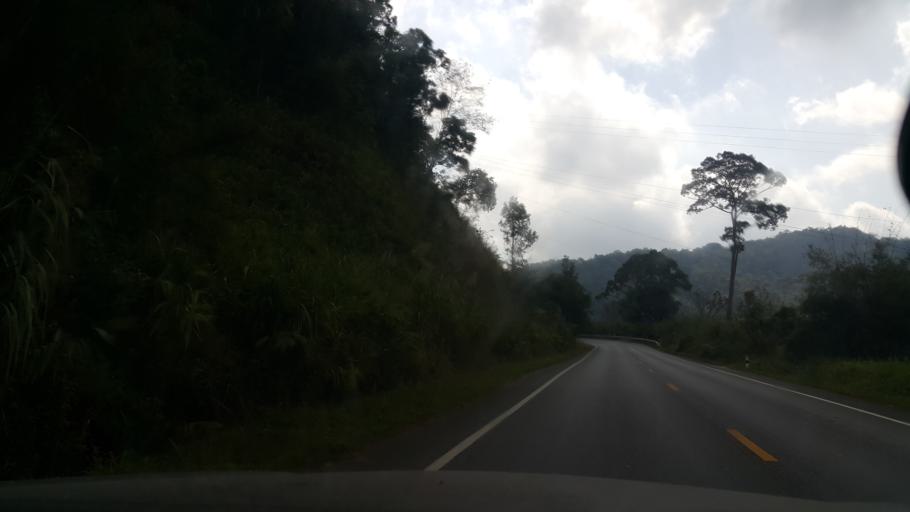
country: TH
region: Phayao
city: Phayao
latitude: 19.0688
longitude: 99.7723
